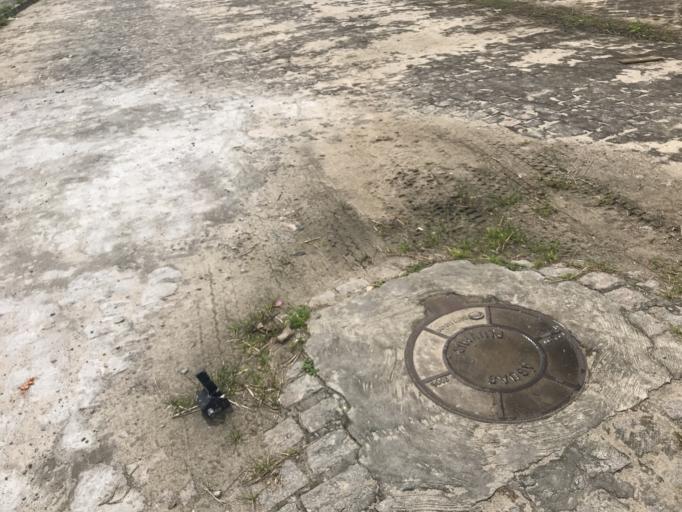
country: BR
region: Bahia
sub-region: Santo Antonio De Jesus
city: Santo Antonio de Jesus
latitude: -12.9796
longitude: -39.2823
